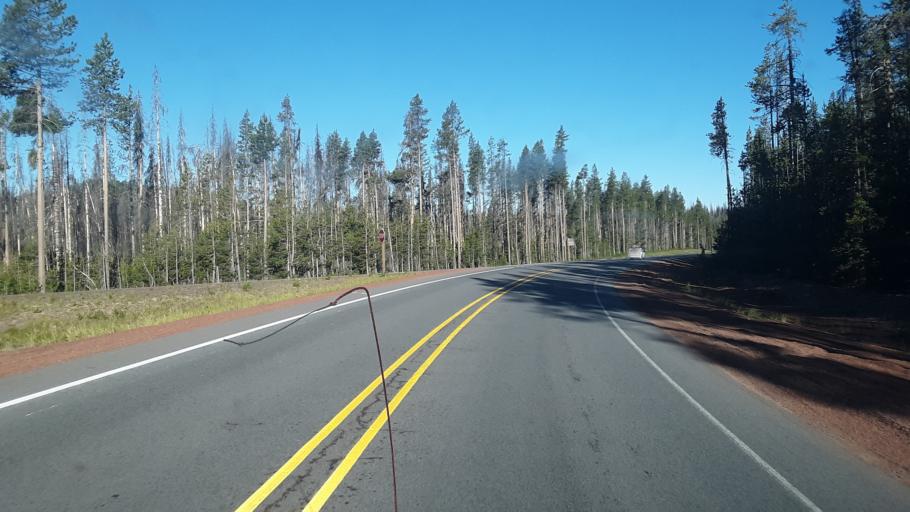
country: US
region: Oregon
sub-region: Lane County
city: Oakridge
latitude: 43.0890
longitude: -122.1164
